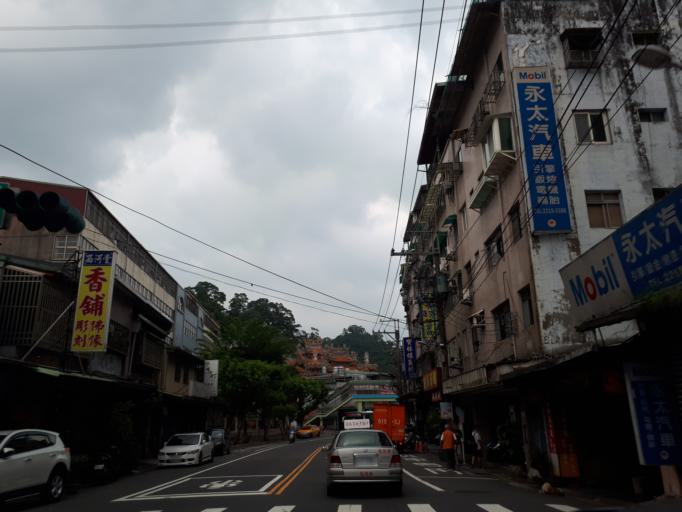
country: TW
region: Taipei
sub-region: Taipei
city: Banqiao
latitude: 24.9516
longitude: 121.4860
